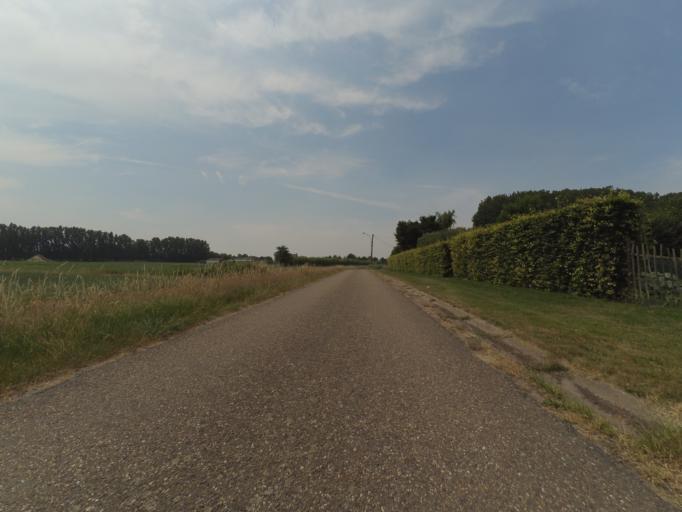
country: BE
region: Flanders
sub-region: Provincie Antwerpen
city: Brecht
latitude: 51.3998
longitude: 4.6581
